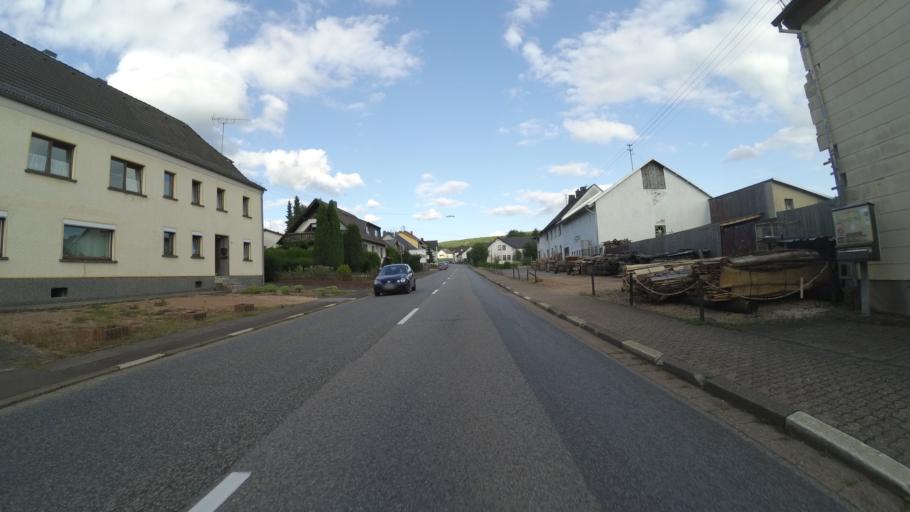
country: DE
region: Saarland
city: Tholey
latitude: 49.5391
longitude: 6.9793
